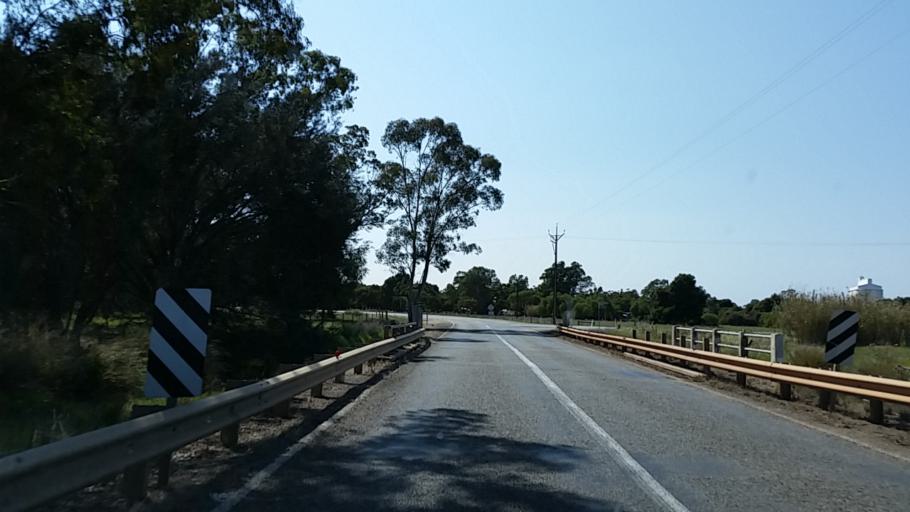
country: AU
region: South Australia
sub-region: Northern Areas
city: Jamestown
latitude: -33.1822
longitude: 138.4767
